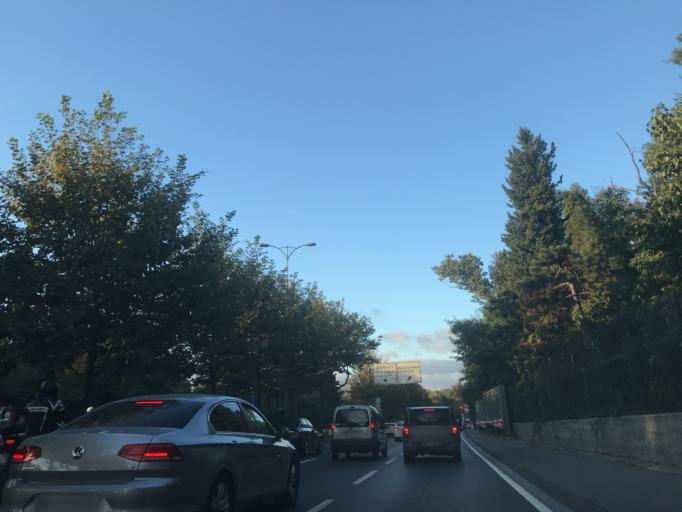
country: TR
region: Istanbul
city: Sisli
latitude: 41.1248
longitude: 29.0238
